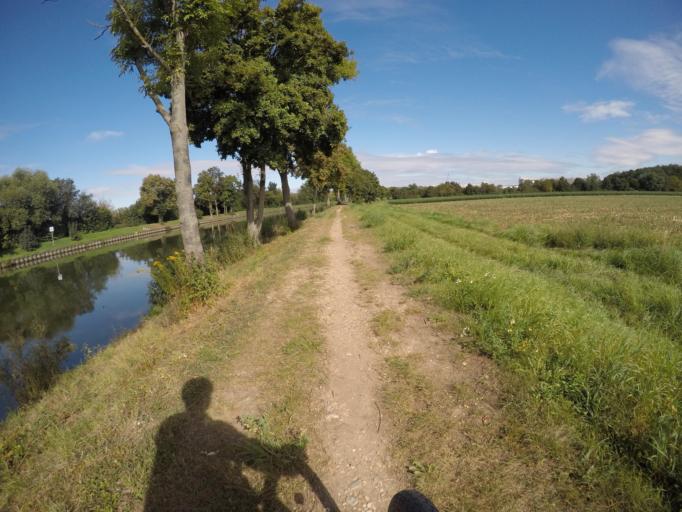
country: DE
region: Baden-Wuerttemberg
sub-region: Regierungsbezirk Stuttgart
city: Pleidelsheim
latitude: 48.9476
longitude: 9.1923
